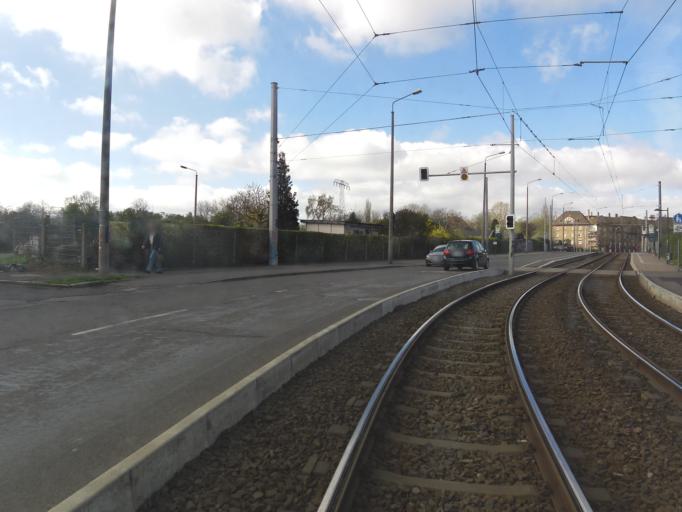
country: DE
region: Saxony
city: Leipzig
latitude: 51.3144
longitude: 12.3165
